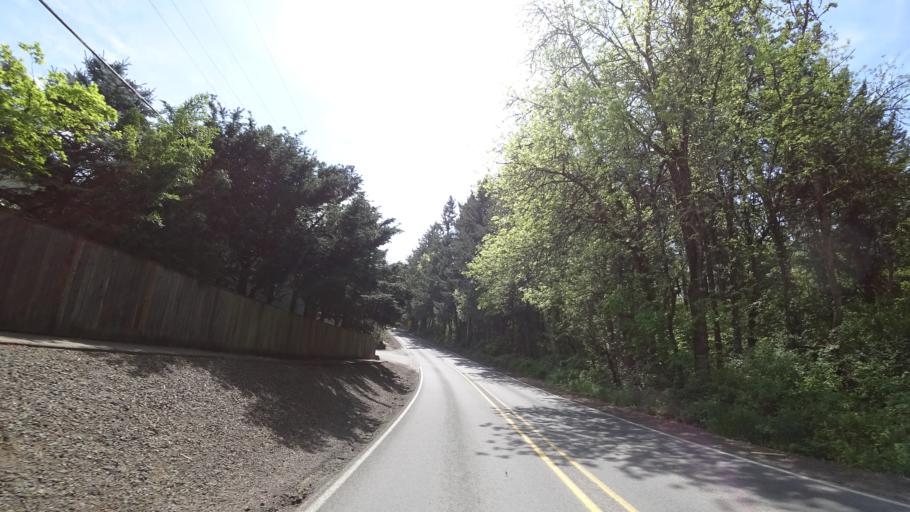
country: US
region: Oregon
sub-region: Washington County
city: Aloha
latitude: 45.4638
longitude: -122.8921
